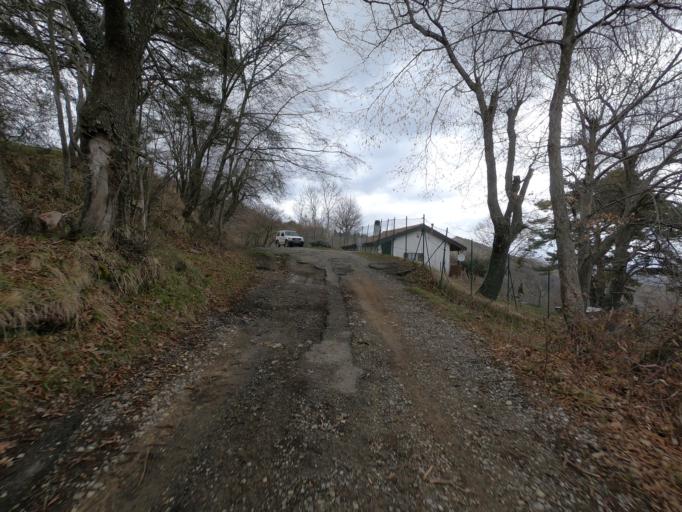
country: IT
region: Liguria
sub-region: Provincia di Imperia
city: Pietrabruna
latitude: 43.9112
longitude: 7.8794
